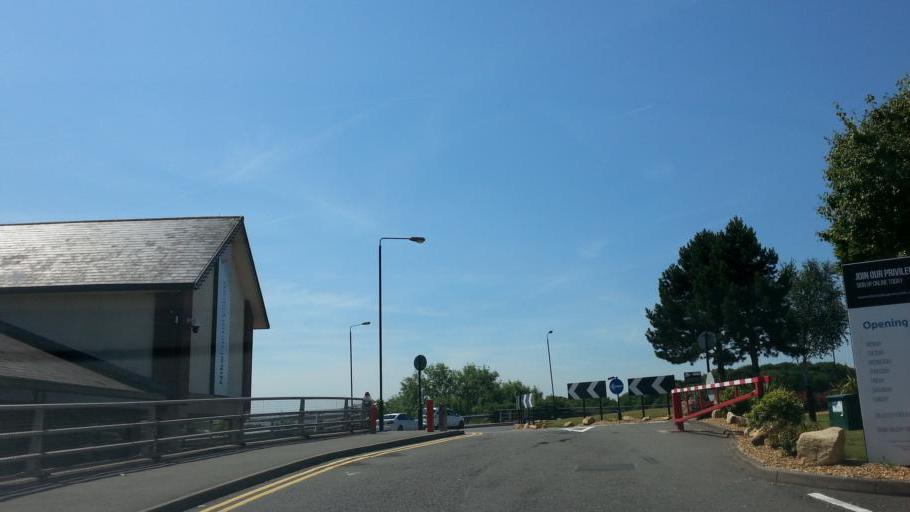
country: GB
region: England
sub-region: Derbyshire
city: Pinxton
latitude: 53.1071
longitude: -1.3123
